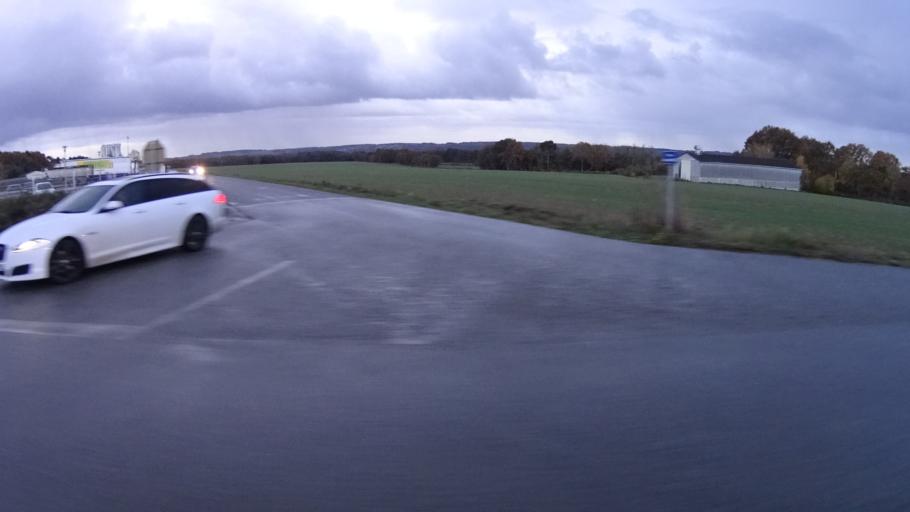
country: FR
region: Brittany
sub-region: Departement d'Ille-et-Vilaine
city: Sainte-Marie
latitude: 47.6970
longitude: -2.0227
